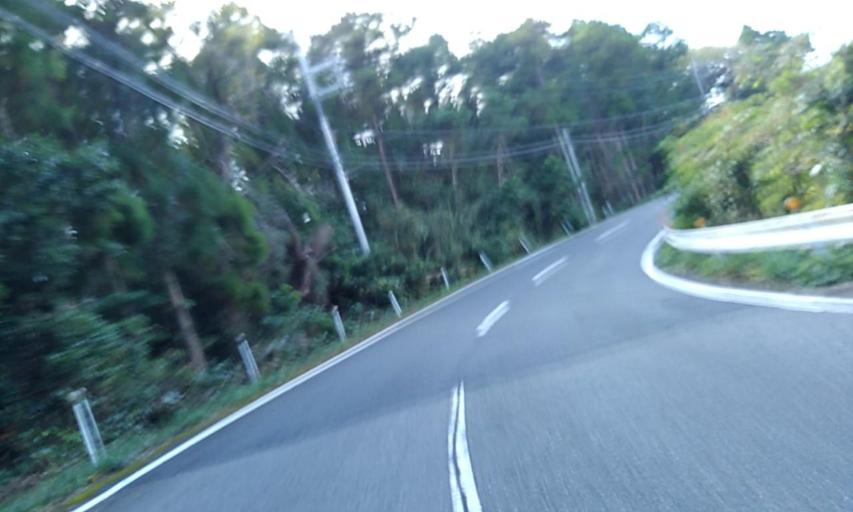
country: JP
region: Wakayama
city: Shingu
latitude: 33.4693
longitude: 135.8444
